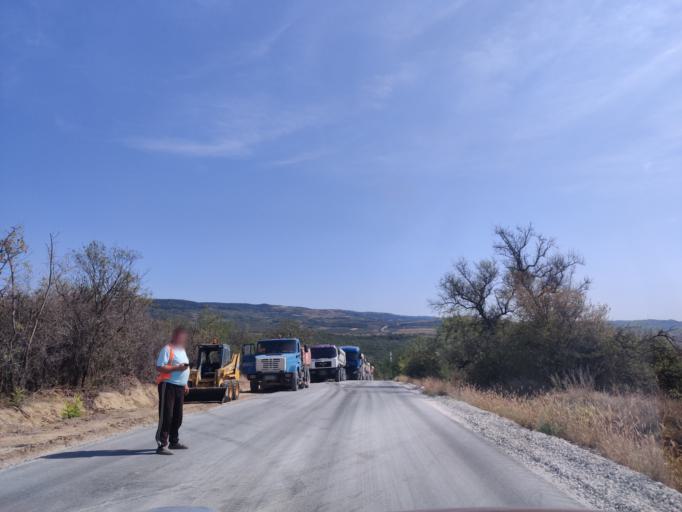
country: MD
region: Ungheni
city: Ungheni
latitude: 47.2580
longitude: 27.9927
